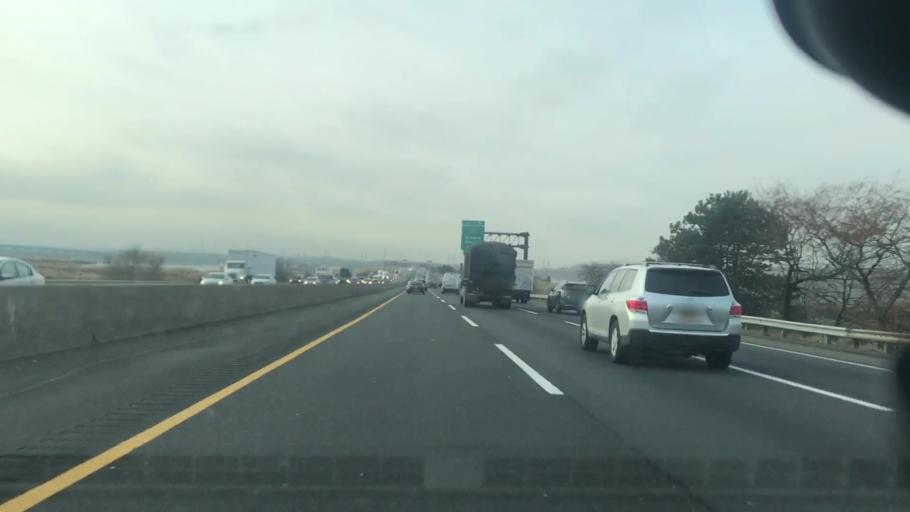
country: US
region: New Jersey
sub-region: Bergen County
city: North Arlington
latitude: 40.7814
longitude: -74.0969
